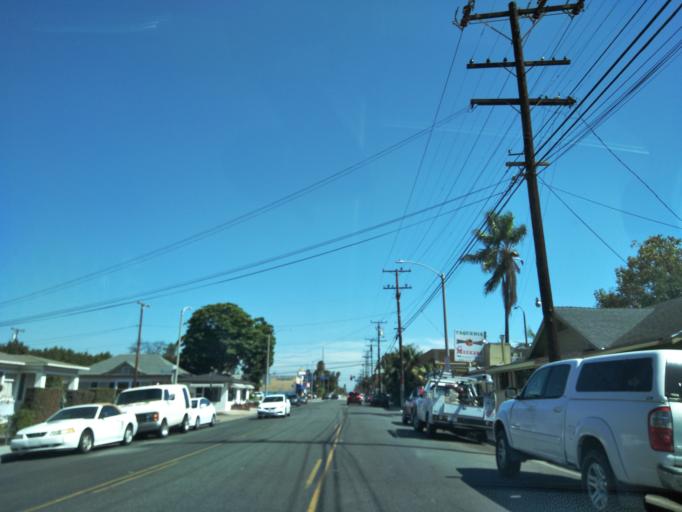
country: US
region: California
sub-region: Los Angeles County
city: Signal Hill
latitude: 33.7717
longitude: -118.1539
